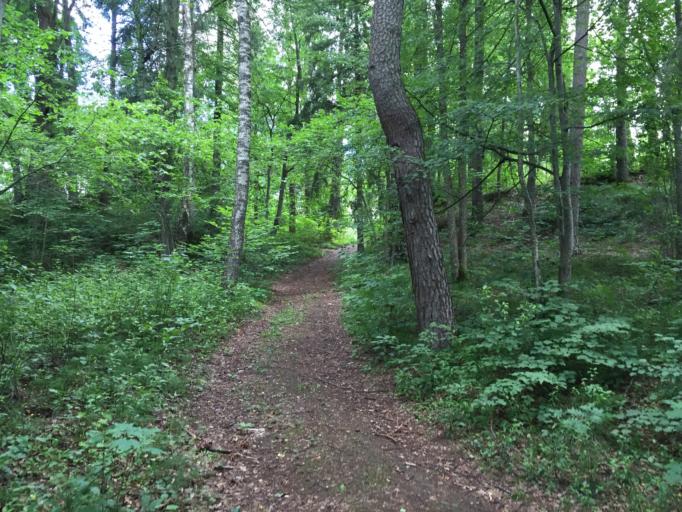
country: LV
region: Ropazu
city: Ropazi
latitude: 56.9670
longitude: 24.5135
